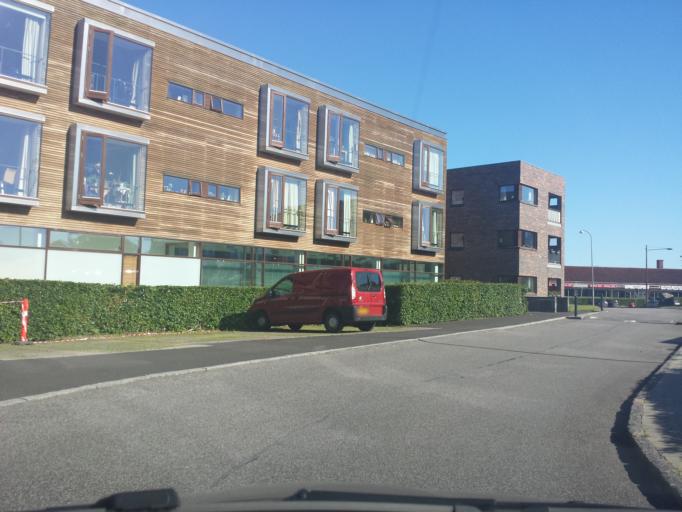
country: DK
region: Capital Region
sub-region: Herlev Kommune
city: Herlev
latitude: 55.7226
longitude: 12.4012
